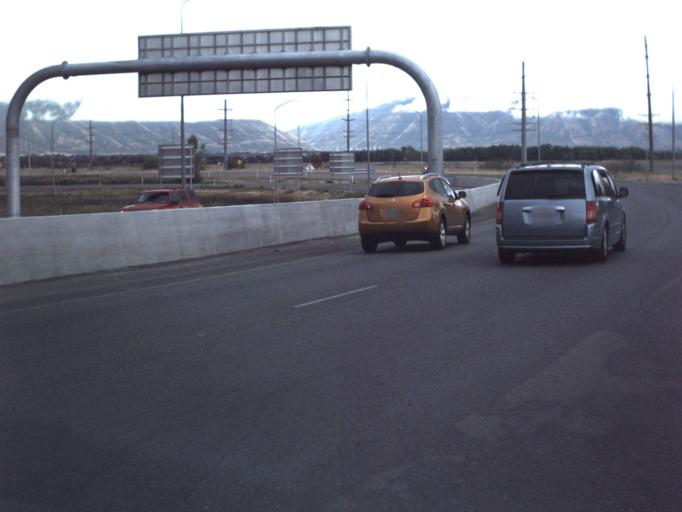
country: US
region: Utah
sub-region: Utah County
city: Provo
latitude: 40.2070
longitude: -111.6612
